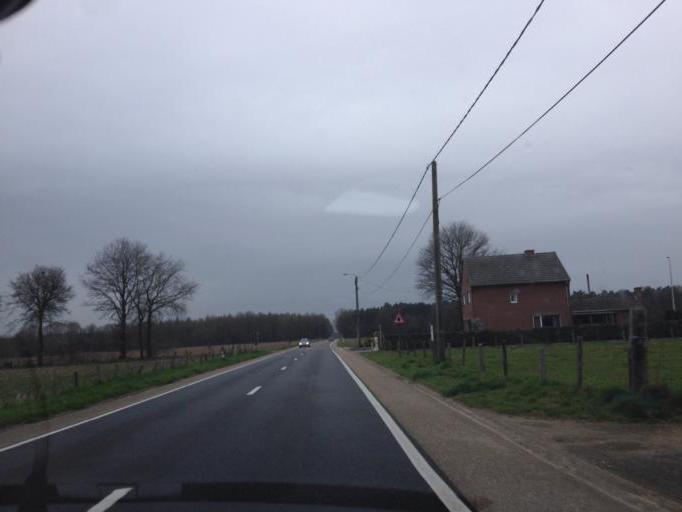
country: BE
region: Flanders
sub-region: Provincie Limburg
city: Opglabbeek
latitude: 51.0750
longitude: 5.5542
